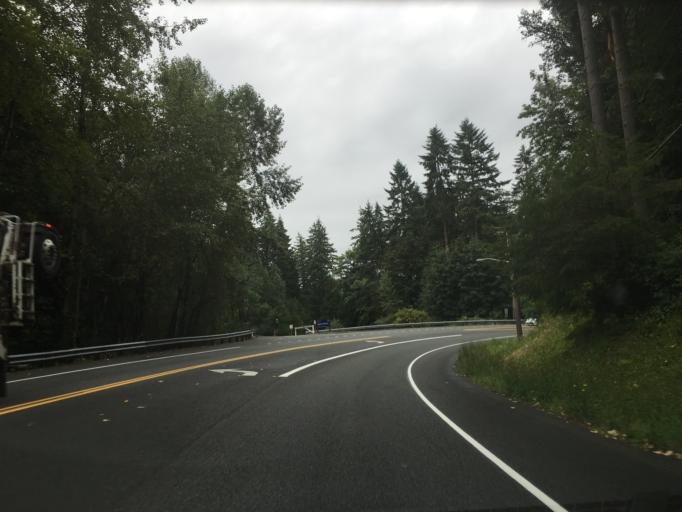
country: US
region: Washington
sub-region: King County
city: Inglewood-Finn Hill
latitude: 47.7249
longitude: -122.2416
